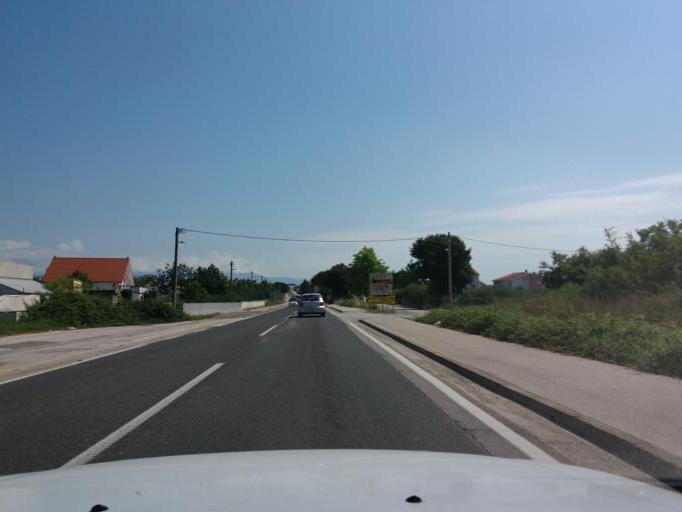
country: HR
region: Zadarska
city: Policnik
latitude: 44.1421
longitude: 15.3159
